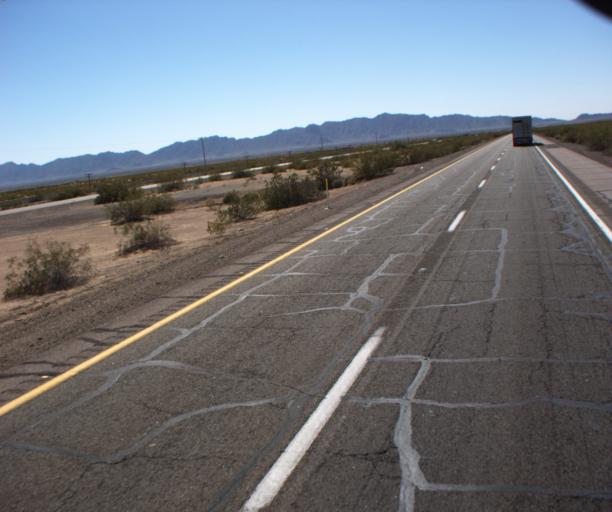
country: US
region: Arizona
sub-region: Yuma County
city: Wellton
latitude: 32.7663
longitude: -113.6215
